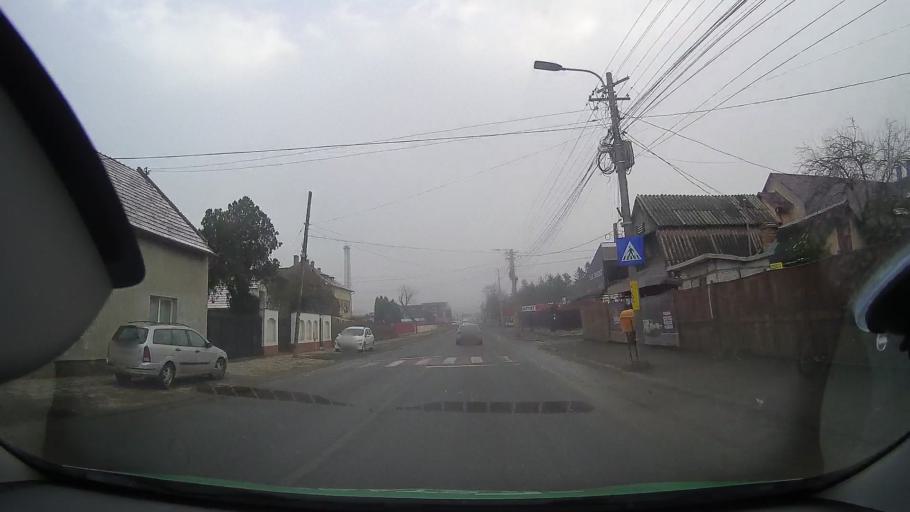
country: RO
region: Mures
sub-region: Municipiul Tarnaveni
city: Tarnaveni
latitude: 46.3182
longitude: 24.2967
